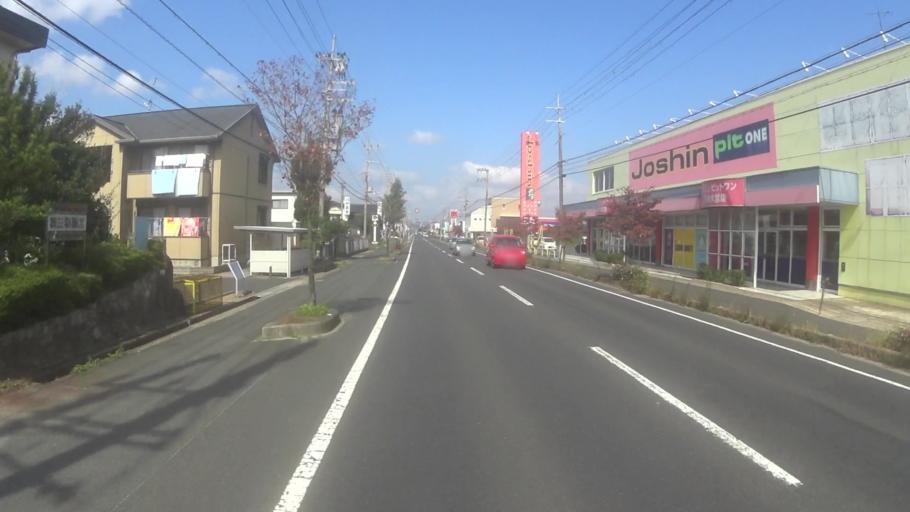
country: JP
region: Kyoto
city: Miyazu
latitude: 35.5941
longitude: 135.0916
